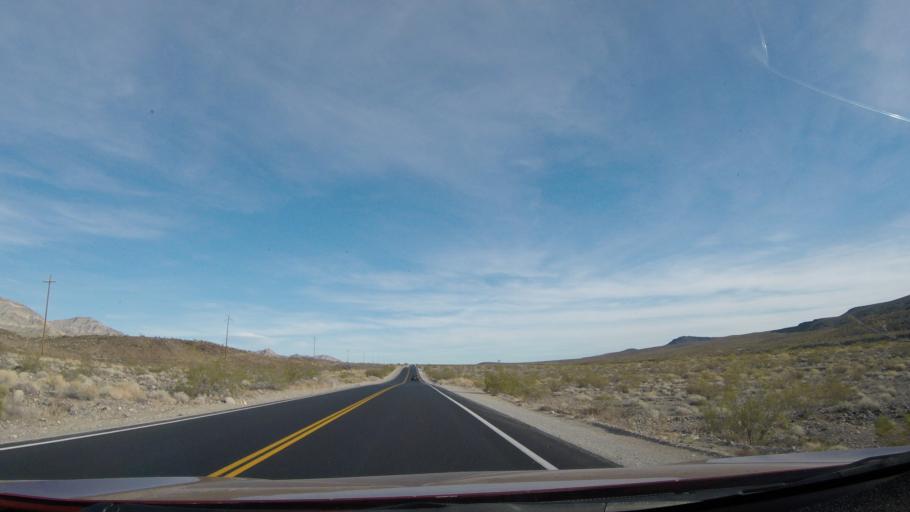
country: US
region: Nevada
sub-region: Nye County
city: Beatty
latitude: 36.3510
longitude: -116.6354
